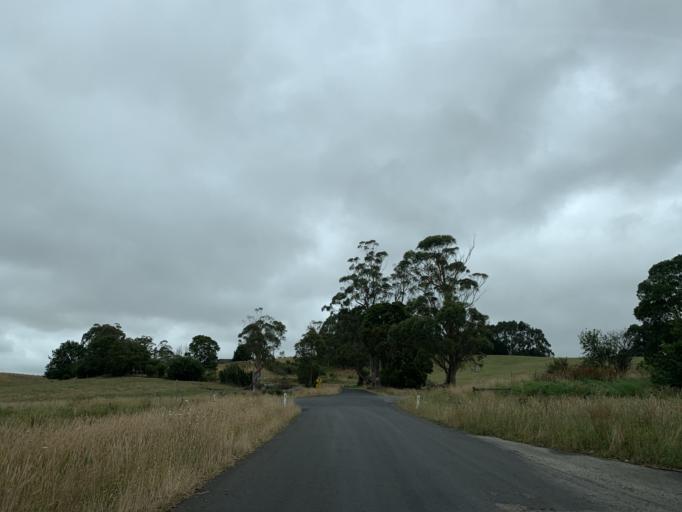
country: AU
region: Victoria
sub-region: Baw Baw
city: Warragul
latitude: -38.2925
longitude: 145.8321
